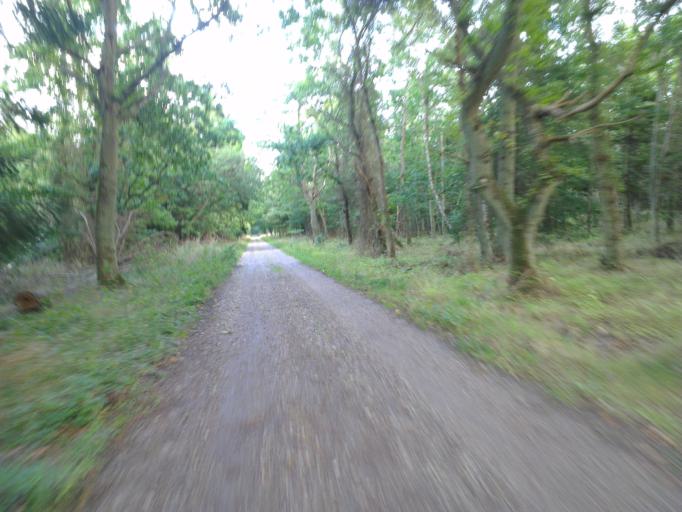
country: DK
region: Capital Region
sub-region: Frederikssund Kommune
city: Jaegerspris
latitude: 55.8465
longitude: 11.9639
